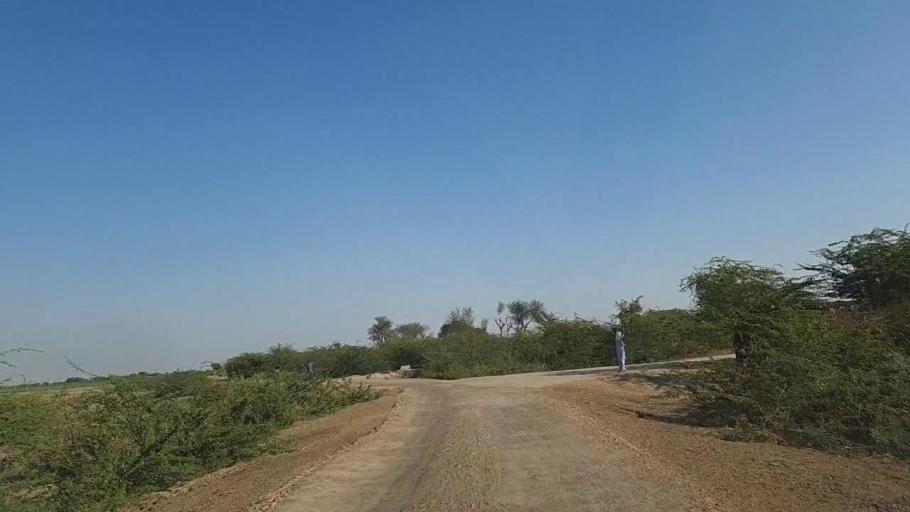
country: PK
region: Sindh
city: Naukot
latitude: 24.9467
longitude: 69.3353
